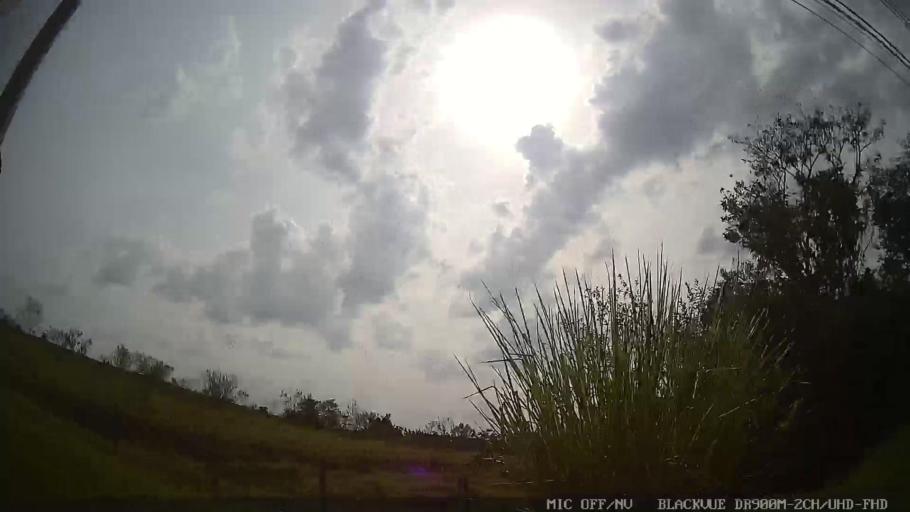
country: BR
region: Sao Paulo
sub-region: Indaiatuba
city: Indaiatuba
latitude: -23.1037
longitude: -47.2640
